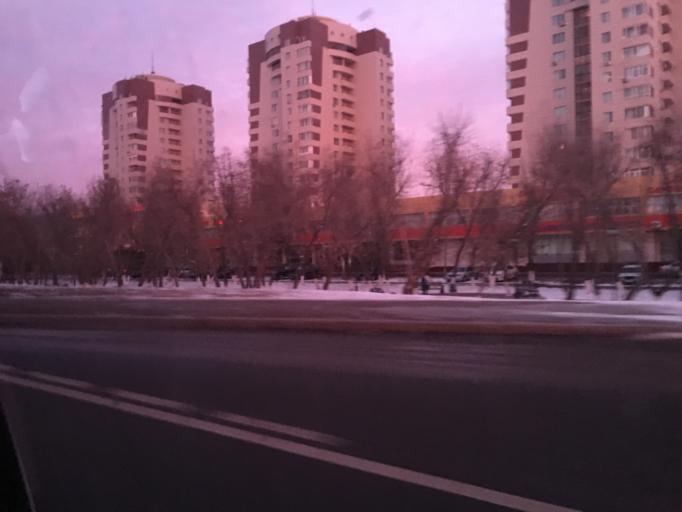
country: KZ
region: Astana Qalasy
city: Astana
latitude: 51.1492
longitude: 71.4250
